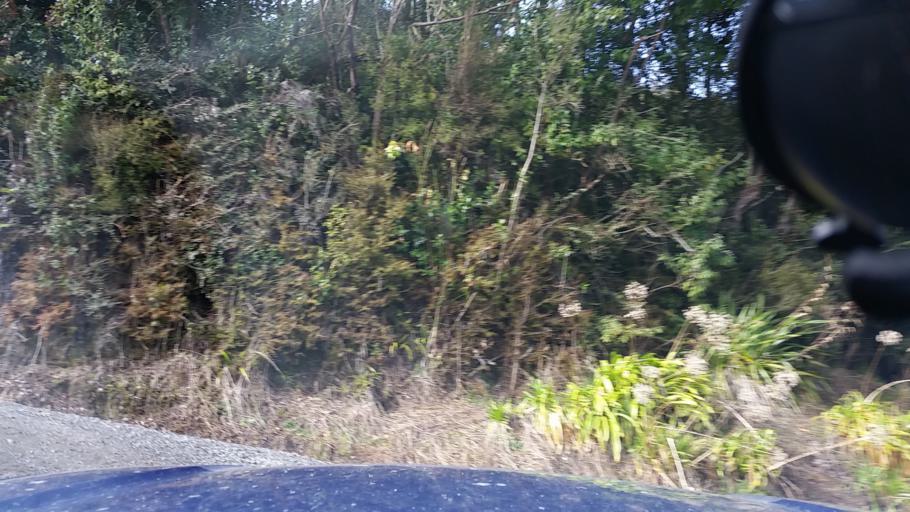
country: NZ
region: Taranaki
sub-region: New Plymouth District
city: Waitara
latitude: -39.0338
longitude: 174.8009
